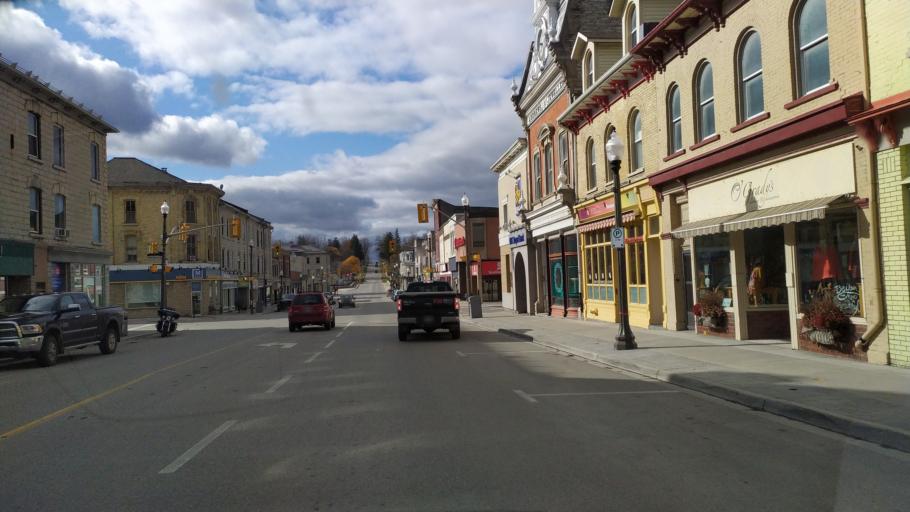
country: CA
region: Ontario
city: Stratford
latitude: 43.2595
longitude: -81.1415
